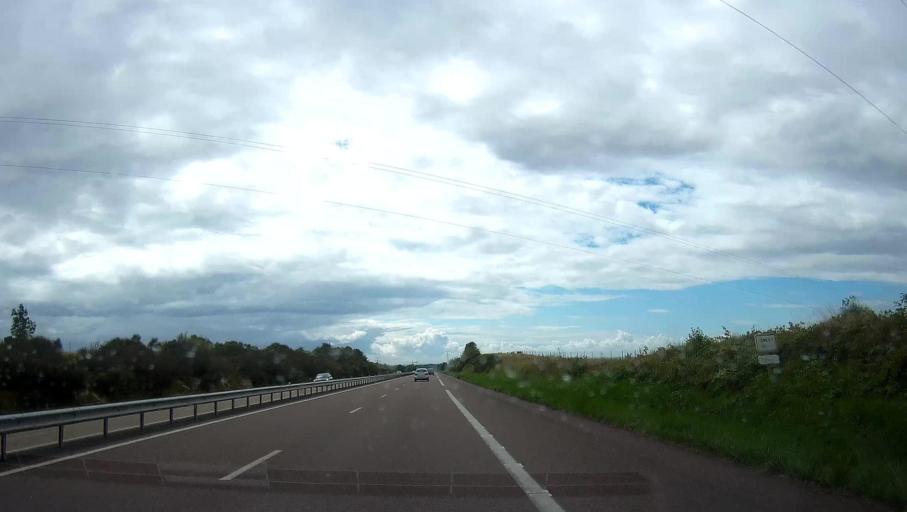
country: FR
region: Champagne-Ardenne
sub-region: Departement de l'Aube
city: Creney-pres-Troyes
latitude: 48.3536
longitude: 4.1643
